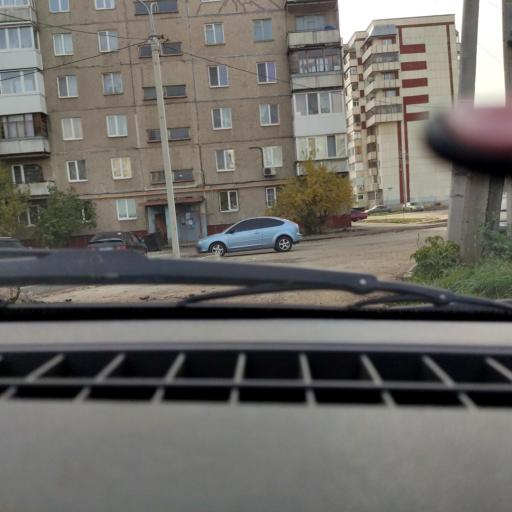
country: RU
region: Bashkortostan
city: Ufa
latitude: 54.8181
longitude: 56.1301
